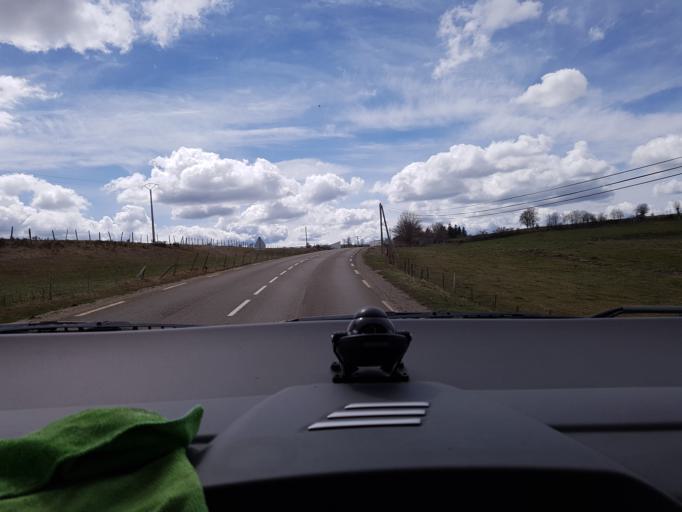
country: FR
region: Midi-Pyrenees
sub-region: Departement de l'Aveyron
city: Laguiole
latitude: 44.7750
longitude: 2.8953
